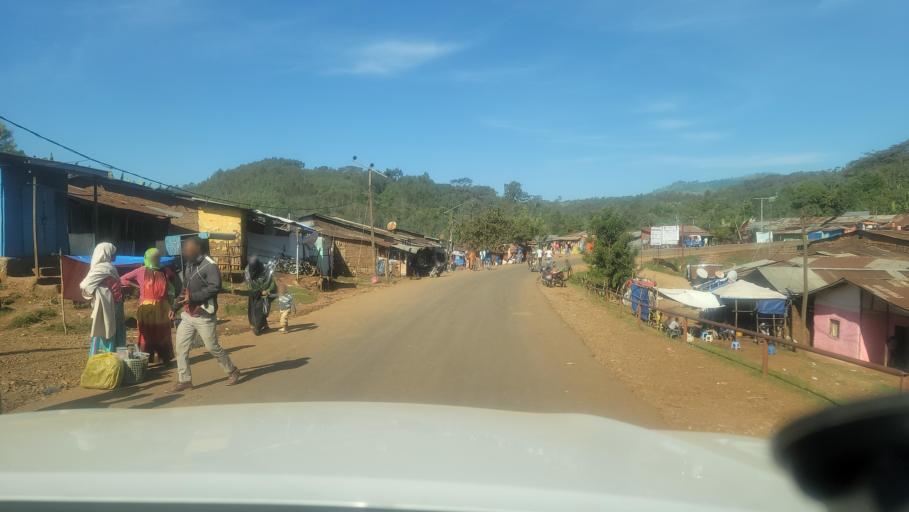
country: ET
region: Oromiya
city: Agaro
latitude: 7.7952
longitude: 36.4781
